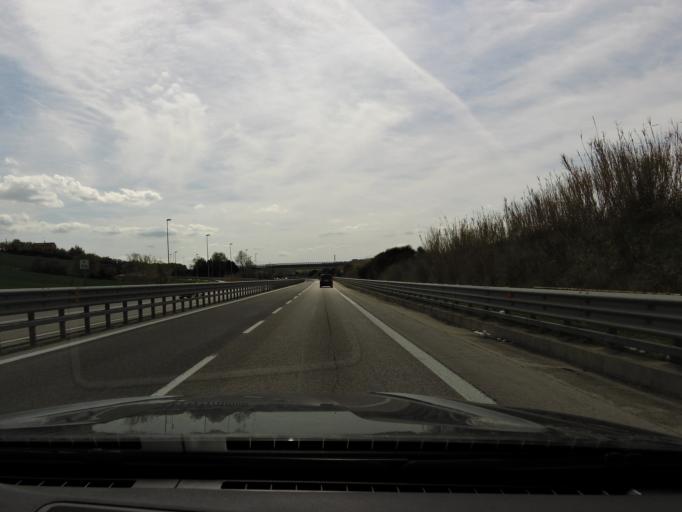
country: IT
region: The Marches
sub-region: Provincia di Ancona
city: San Biagio
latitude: 43.5463
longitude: 13.5152
